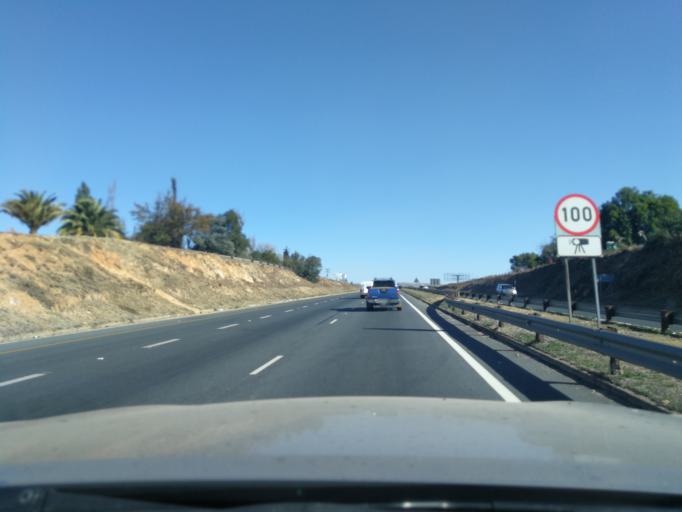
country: ZA
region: Gauteng
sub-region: West Rand District Municipality
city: Muldersdriseloop
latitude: -26.0395
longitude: 27.8444
